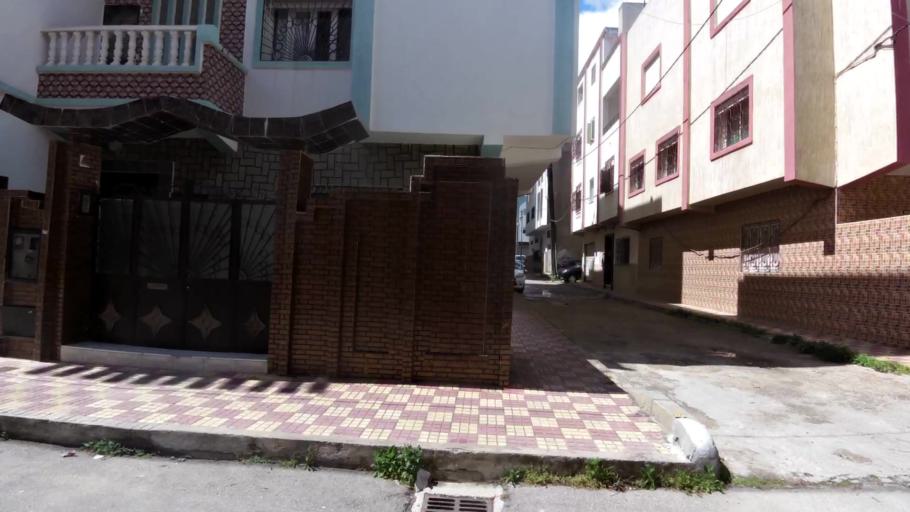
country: MA
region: Tanger-Tetouan
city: Tetouan
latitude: 35.5788
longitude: -5.3437
